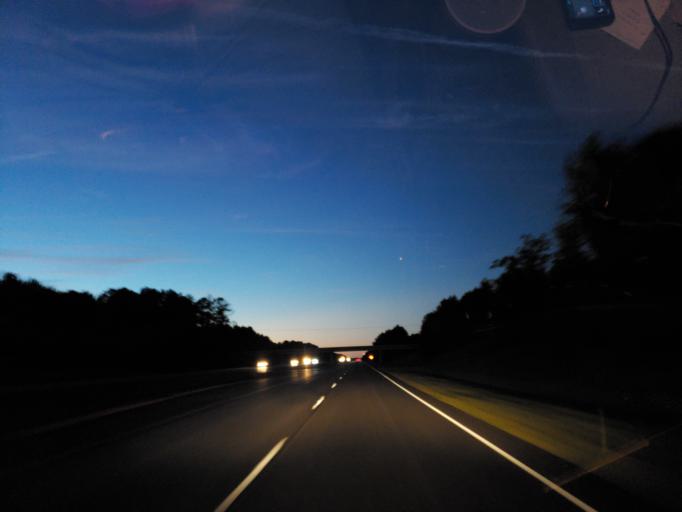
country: US
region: Mississippi
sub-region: Clarke County
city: Quitman
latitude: 32.0748
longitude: -88.6879
